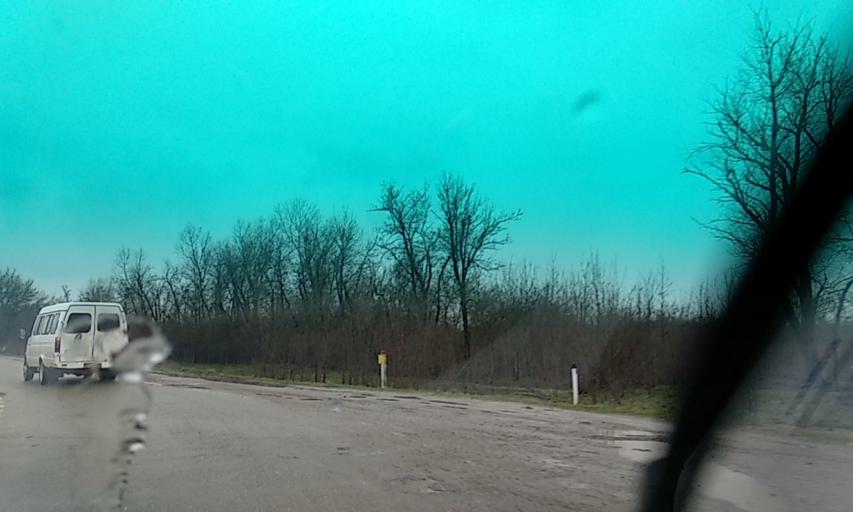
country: RU
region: Krasnodarskiy
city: Belorechensk
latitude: 44.8118
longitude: 39.8527
